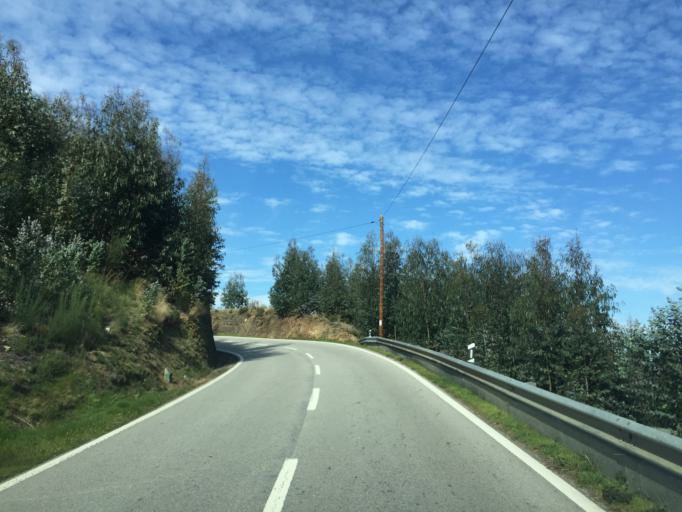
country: PT
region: Aveiro
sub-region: Arouca
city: Arouca
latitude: 40.9584
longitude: -8.1996
